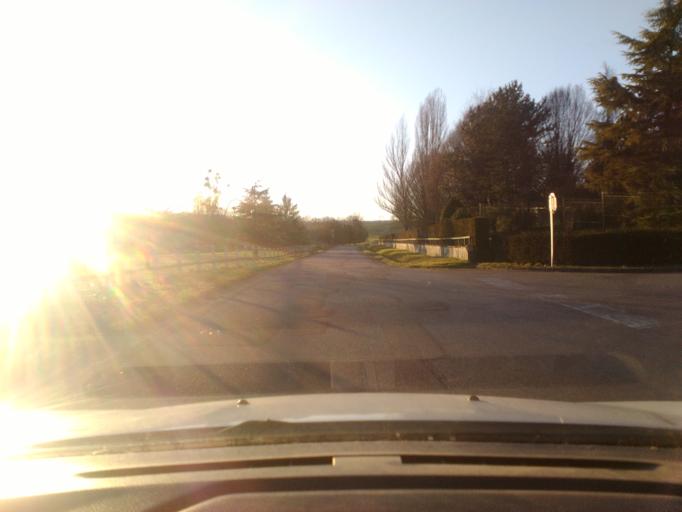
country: FR
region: Lorraine
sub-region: Departement des Vosges
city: Mirecourt
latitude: 48.2975
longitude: 6.1077
